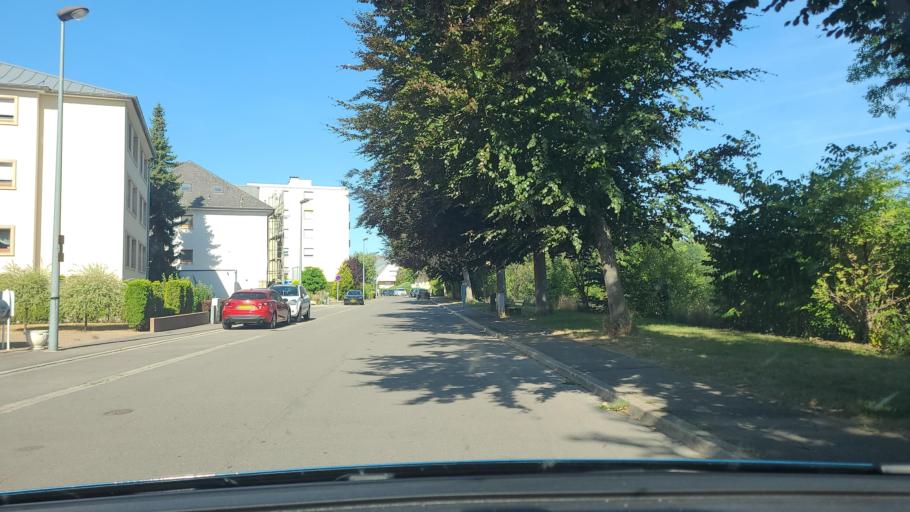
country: LU
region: Luxembourg
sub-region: Canton de Luxembourg
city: Luxembourg
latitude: 49.6000
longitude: 6.1474
